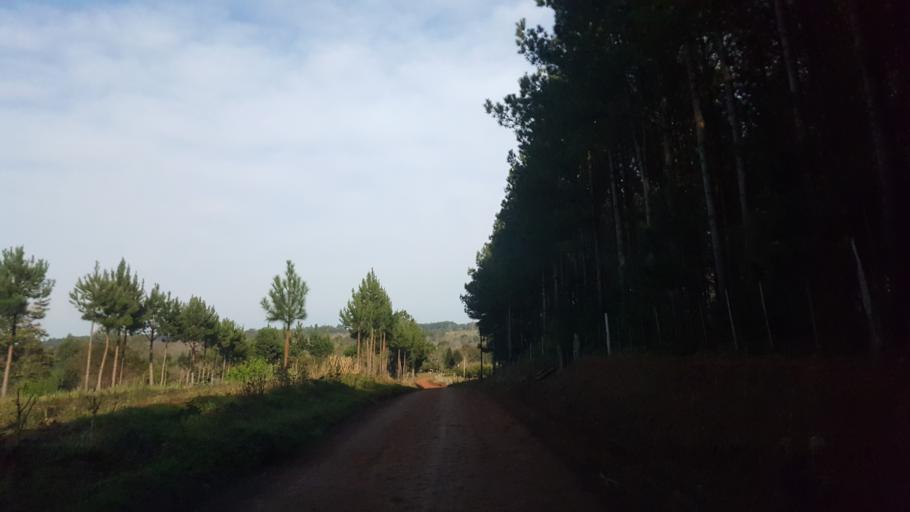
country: AR
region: Misiones
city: Capiovi
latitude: -26.9148
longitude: -55.0750
